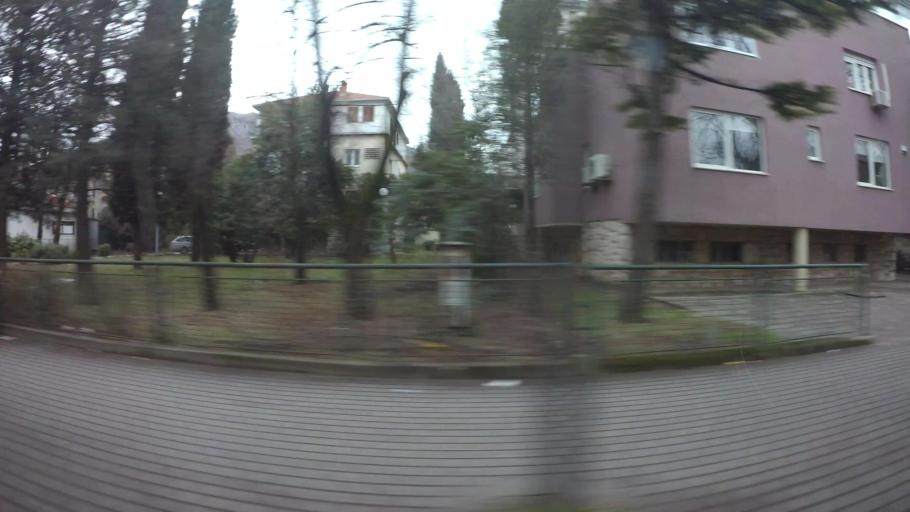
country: BA
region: Federation of Bosnia and Herzegovina
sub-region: Hercegovacko-Bosanski Kanton
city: Mostar
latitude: 43.3407
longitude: 17.8063
